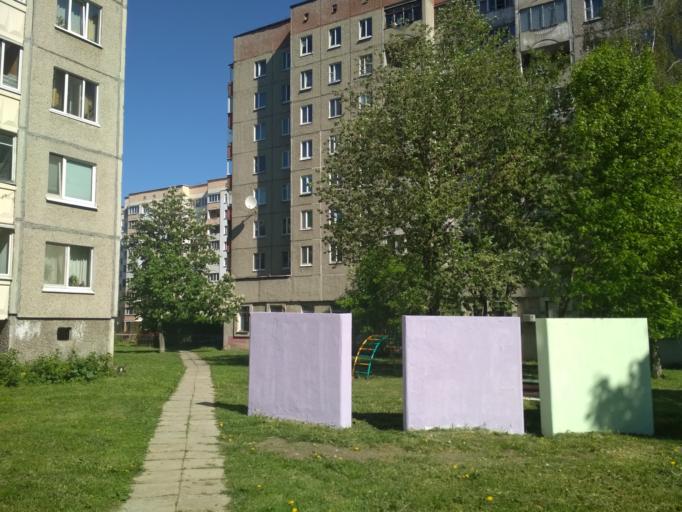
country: BY
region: Minsk
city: Minsk
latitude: 53.8803
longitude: 27.5402
